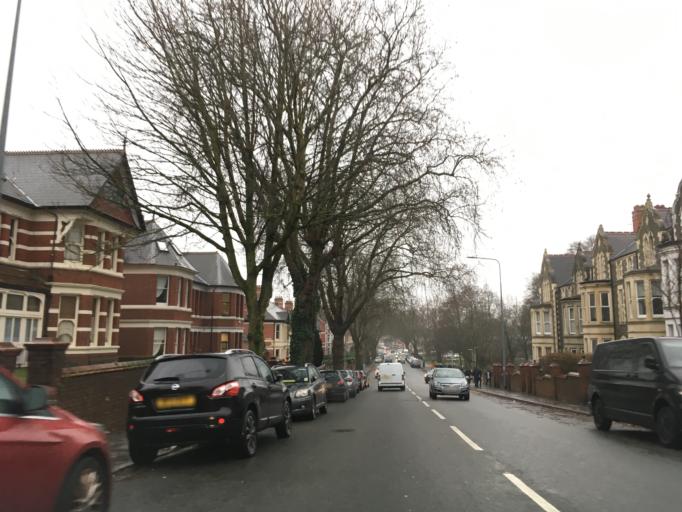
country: GB
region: Wales
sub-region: Cardiff
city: Cardiff
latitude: 51.4985
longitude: -3.1625
